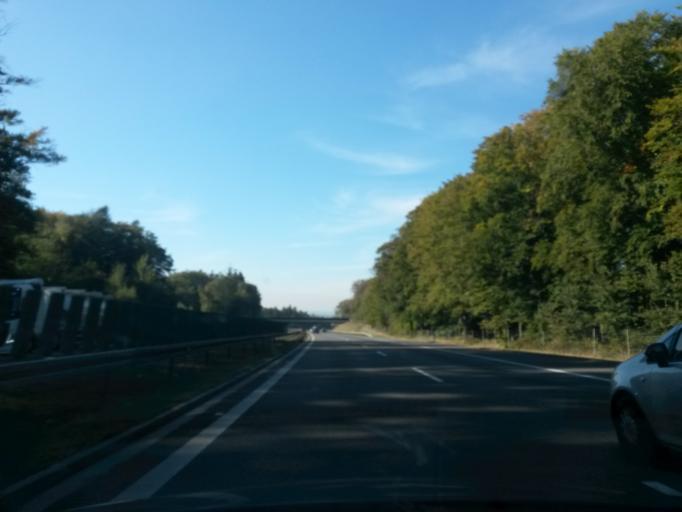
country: PL
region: Opole Voivodeship
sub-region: Powiat krapkowicki
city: Zdzieszowice
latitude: 50.4684
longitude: 18.1485
